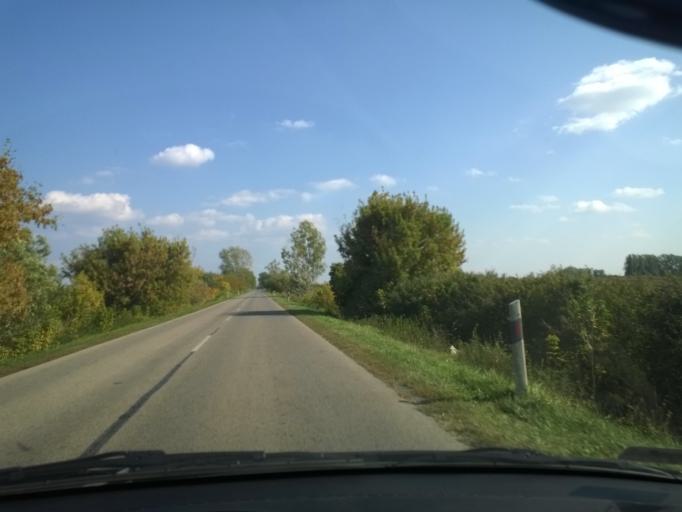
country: HU
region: Bacs-Kiskun
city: Kalocsa
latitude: 46.5097
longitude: 19.0228
